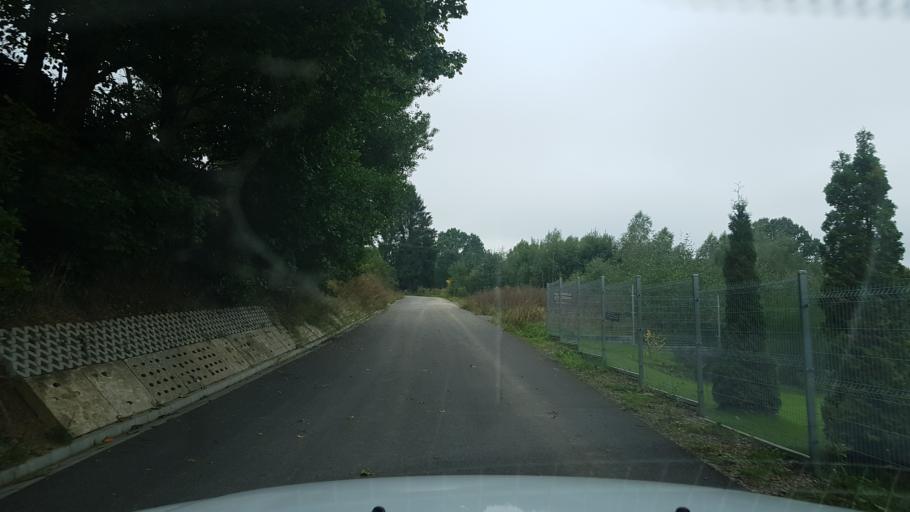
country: PL
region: West Pomeranian Voivodeship
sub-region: Powiat swidwinski
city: Polczyn-Zdroj
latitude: 53.7819
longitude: 16.0703
